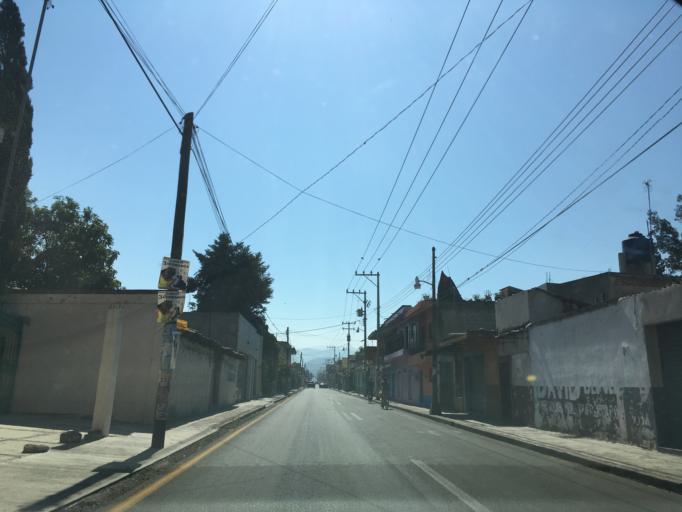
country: MX
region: Michoacan
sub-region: Indaparapeo
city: Colonia de Guadalupe
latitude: 19.8080
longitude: -100.8924
